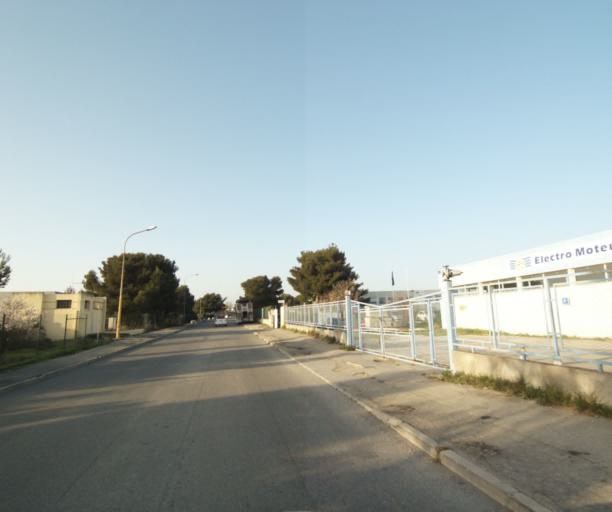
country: FR
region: Provence-Alpes-Cote d'Azur
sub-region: Departement des Bouches-du-Rhone
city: Saint-Victoret
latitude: 43.4373
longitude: 5.2391
